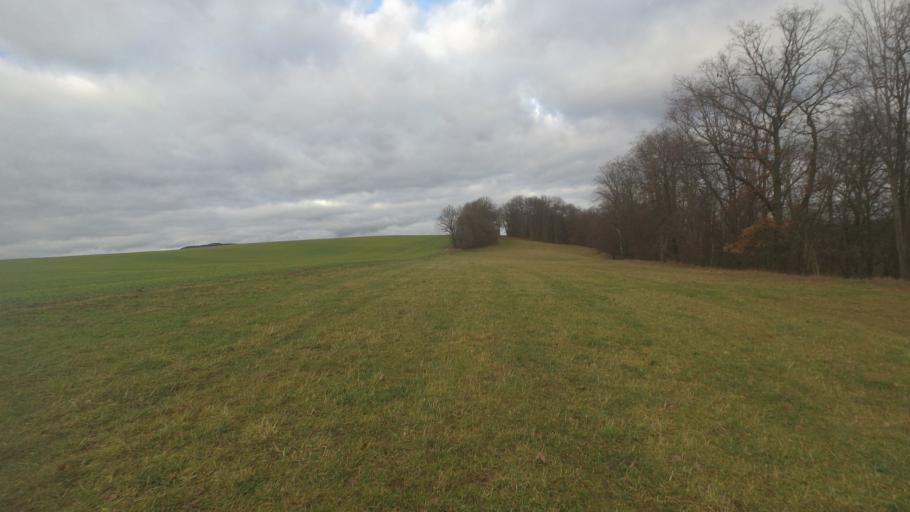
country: DE
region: Thuringia
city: Orlamunde
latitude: 50.7568
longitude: 11.5050
